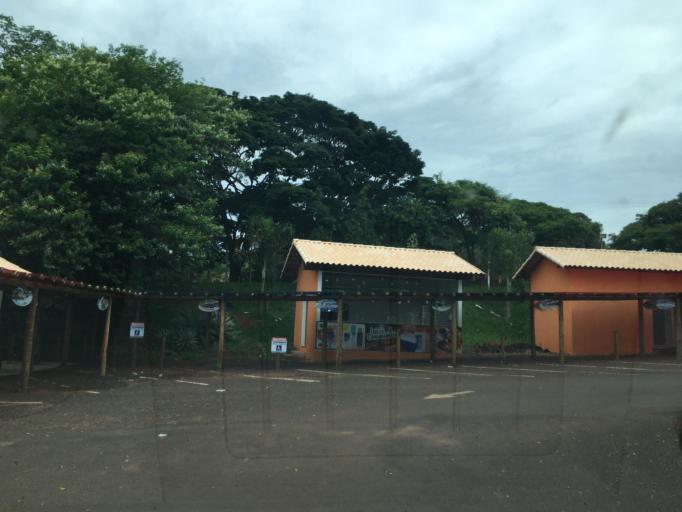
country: BR
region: Minas Gerais
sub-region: Uberlandia
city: Uberlandia
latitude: -18.8653
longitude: -48.2181
